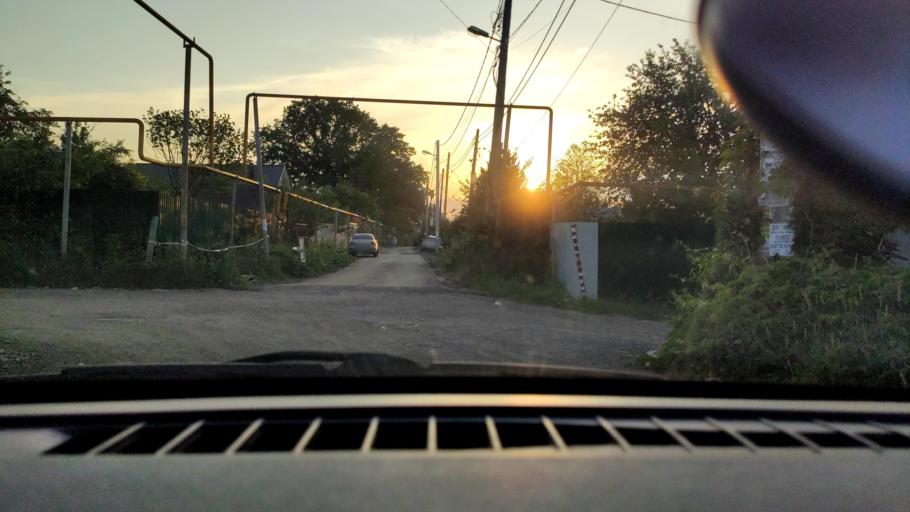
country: RU
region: Samara
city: Samara
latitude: 53.2729
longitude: 50.2157
